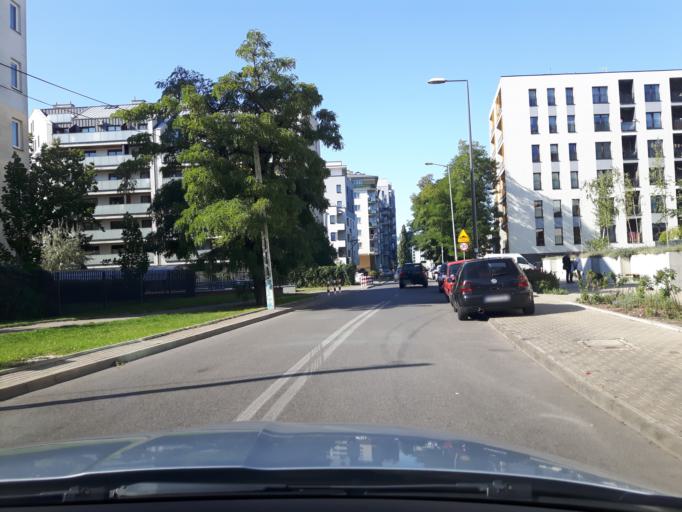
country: PL
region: Masovian Voivodeship
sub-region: Warszawa
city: Praga Poludnie
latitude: 52.2319
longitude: 21.0875
